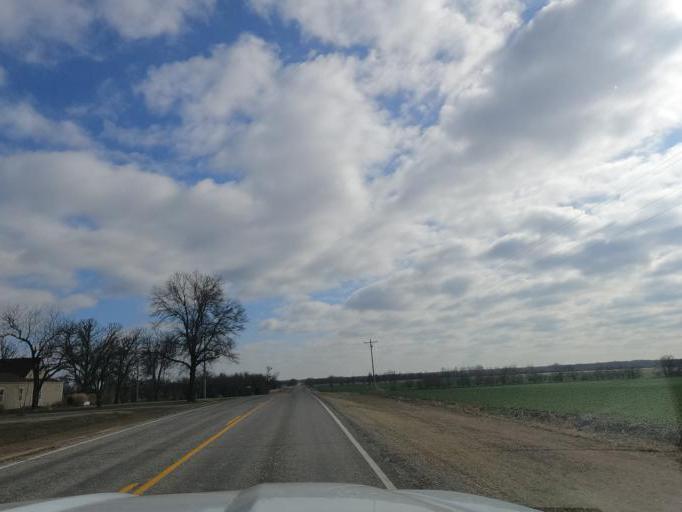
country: US
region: Kansas
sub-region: McPherson County
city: Inman
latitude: 38.1833
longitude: -97.8485
